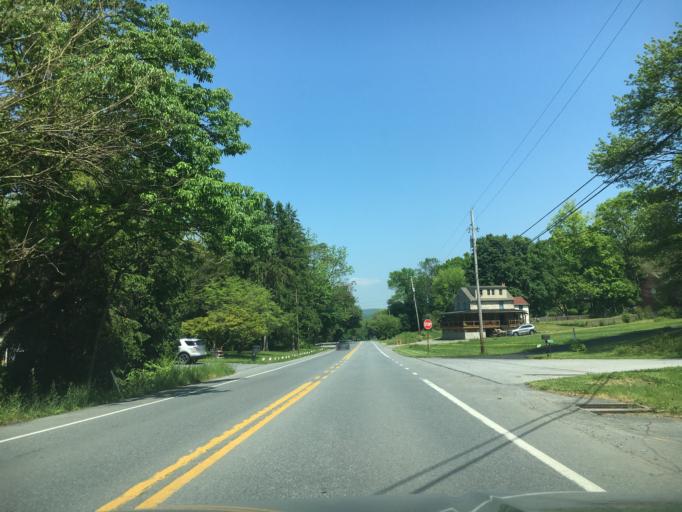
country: US
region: Pennsylvania
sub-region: Berks County
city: Oley
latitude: 40.3757
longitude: -75.7210
